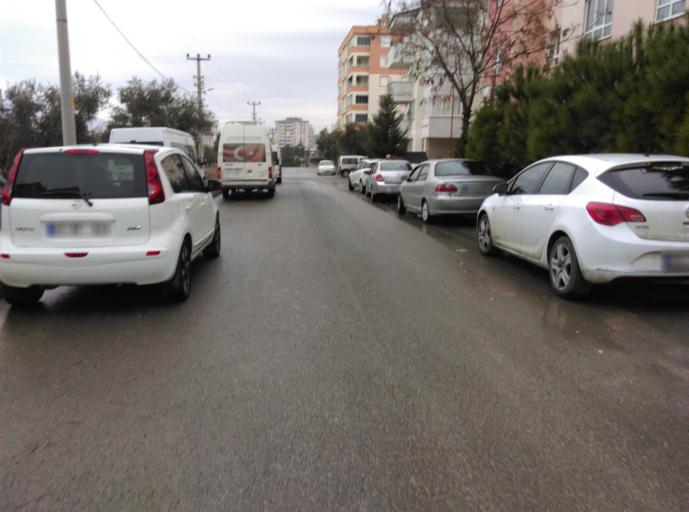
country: TR
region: Kahramanmaras
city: Kahramanmaras
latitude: 37.5819
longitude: 36.8912
